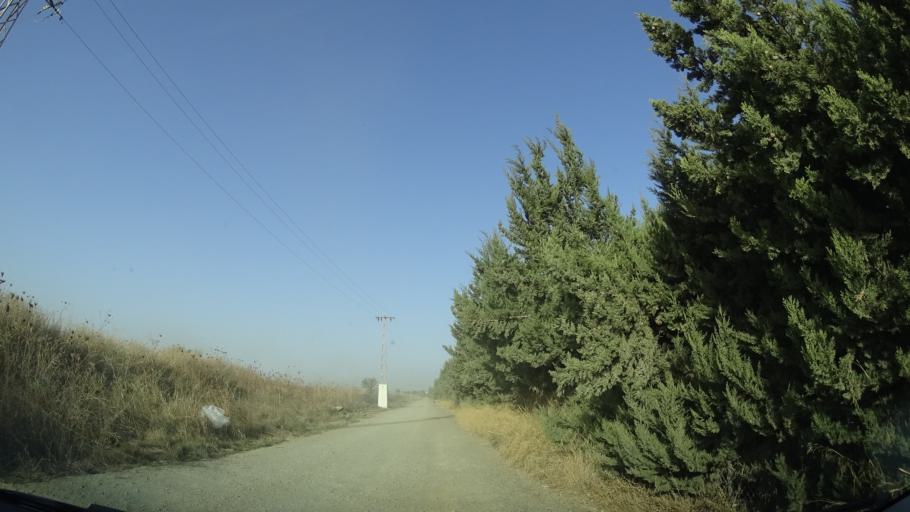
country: ES
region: Andalusia
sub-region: Provincia de Sevilla
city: La Algaba
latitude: 37.4400
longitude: -5.9788
